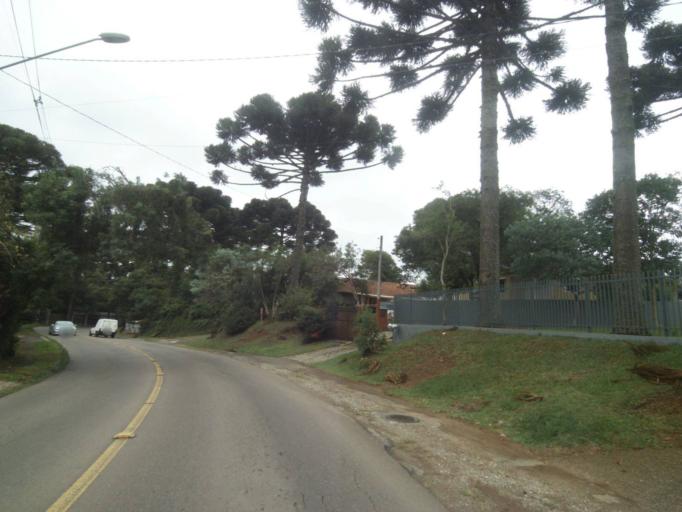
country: BR
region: Parana
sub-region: Curitiba
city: Curitiba
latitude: -25.4489
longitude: -49.3340
